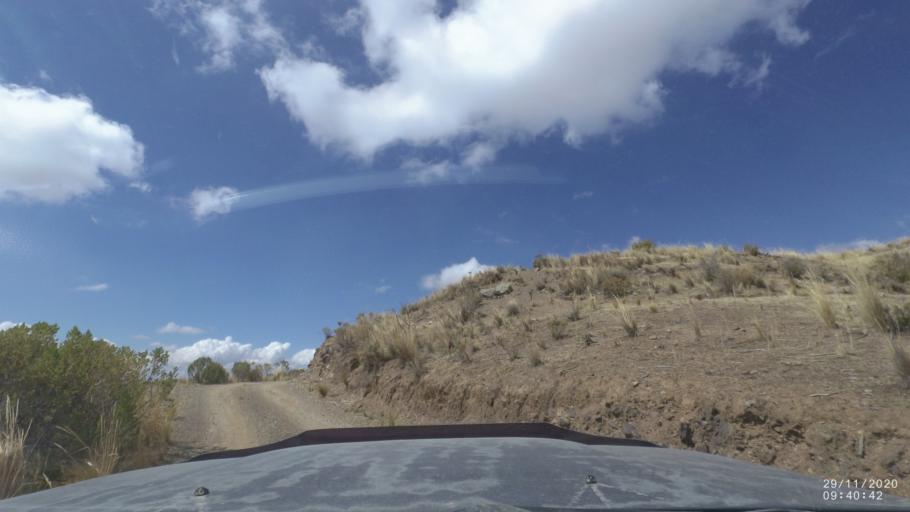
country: BO
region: Cochabamba
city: Cochabamba
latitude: -17.3030
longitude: -66.1811
